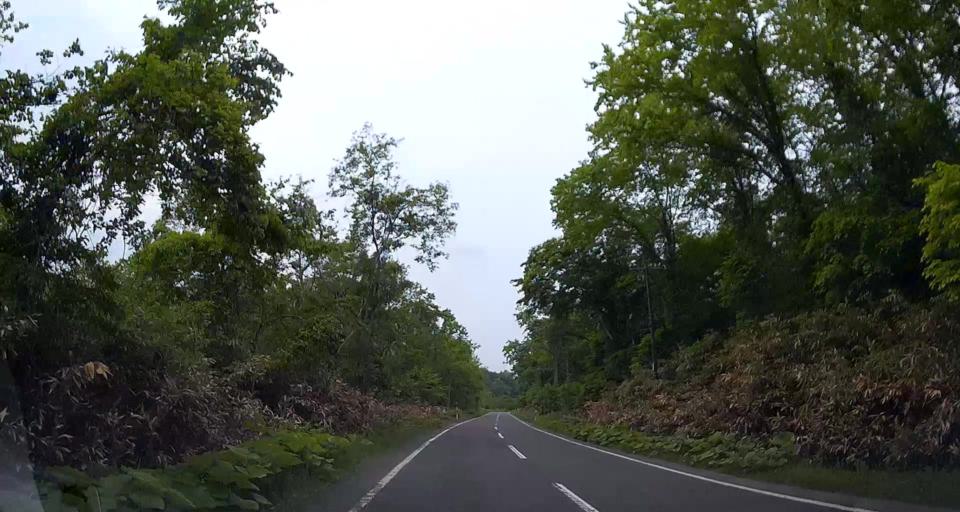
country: JP
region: Hokkaido
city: Shiraoi
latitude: 42.6399
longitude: 141.2274
